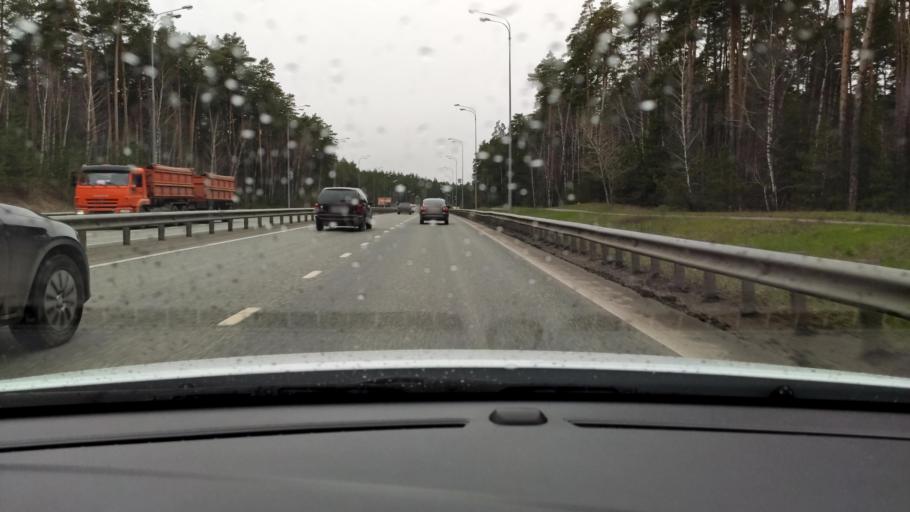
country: RU
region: Tatarstan
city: Staroye Arakchino
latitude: 55.8297
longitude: 48.9961
